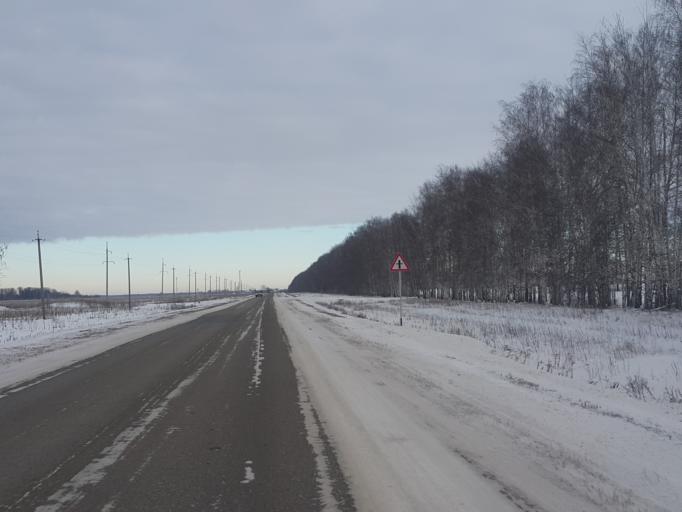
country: RU
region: Tambov
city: Novaya Lyada
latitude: 52.8096
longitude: 41.7893
